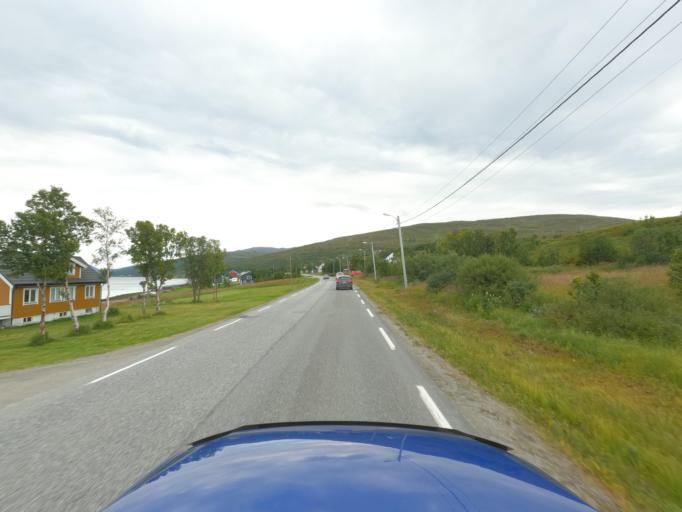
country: NO
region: Finnmark Fylke
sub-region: Kvalsund
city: Kvalsund
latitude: 70.5060
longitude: 24.0543
